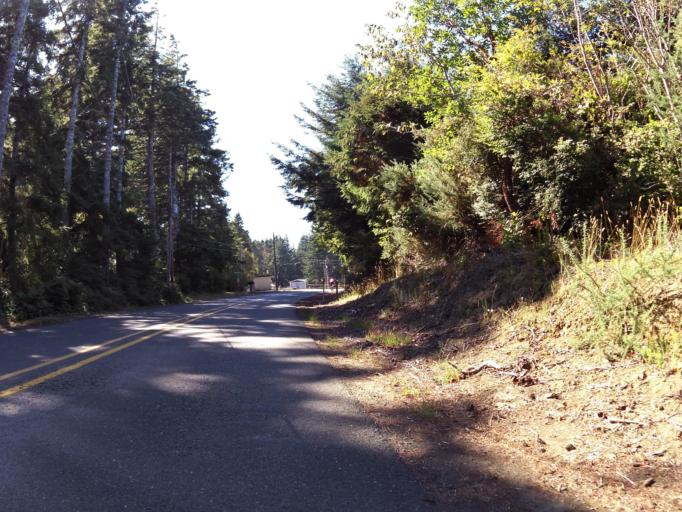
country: US
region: Oregon
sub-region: Coos County
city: Bandon
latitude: 43.2137
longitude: -124.3680
